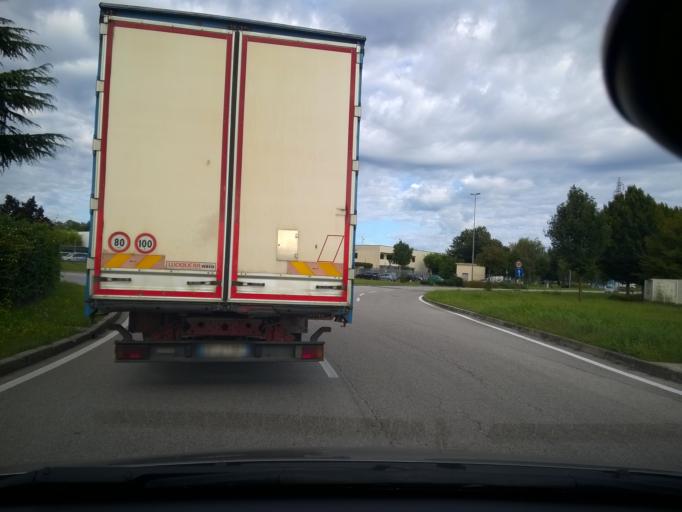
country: IT
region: Friuli Venezia Giulia
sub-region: Provincia di Udine
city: Lauzacco
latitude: 46.0126
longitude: 13.2670
